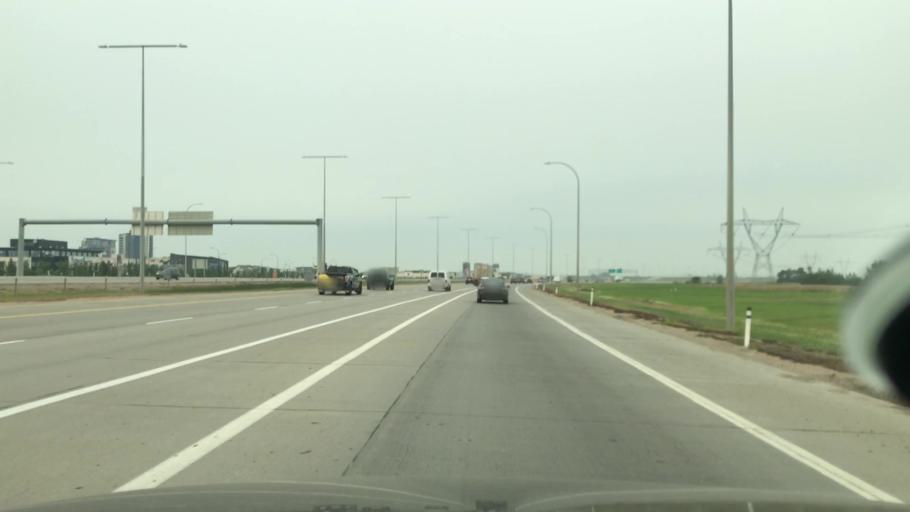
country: CA
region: Alberta
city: Devon
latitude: 53.4321
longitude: -113.5861
